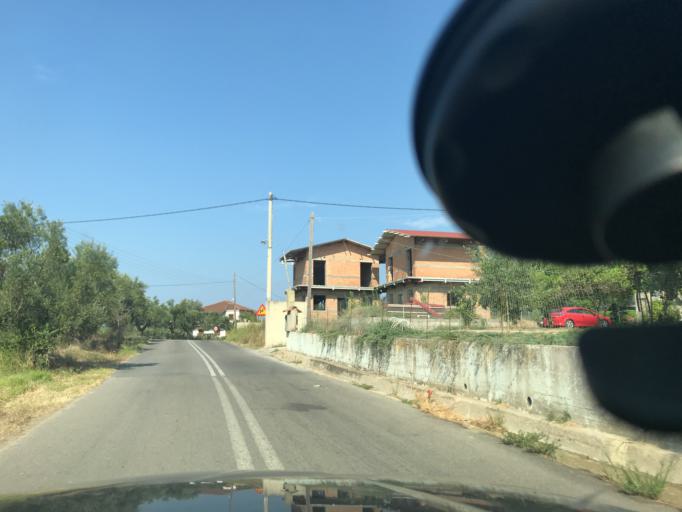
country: GR
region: West Greece
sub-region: Nomos Ileias
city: Kardamas
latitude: 37.7157
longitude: 21.3435
